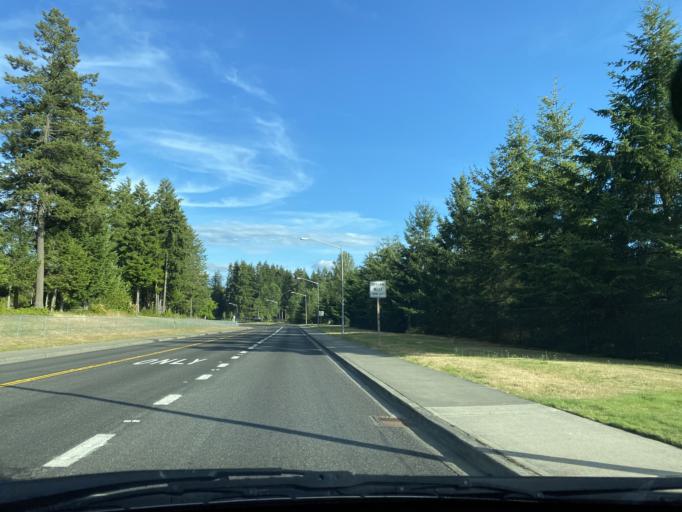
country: US
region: Washington
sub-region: Pierce County
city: Graham
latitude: 47.0901
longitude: -122.2665
